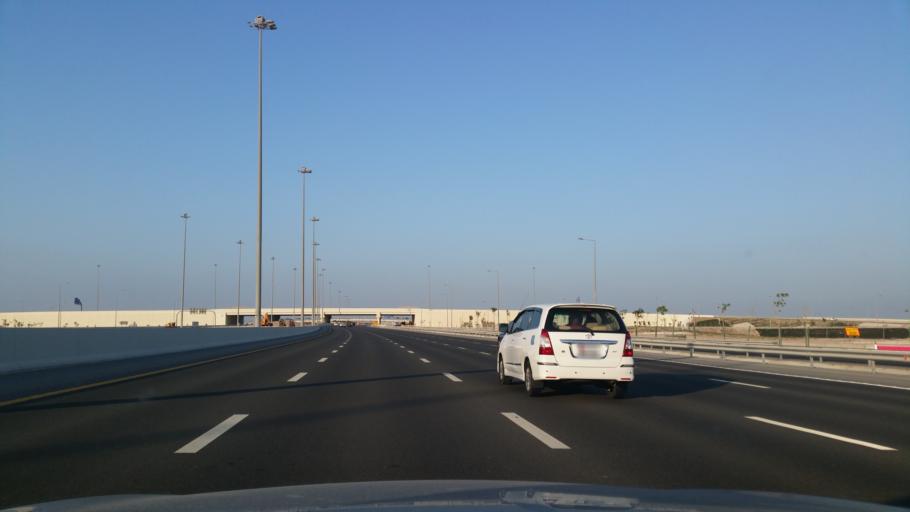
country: QA
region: Al Khawr
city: Al Khawr
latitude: 25.6369
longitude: 51.4915
